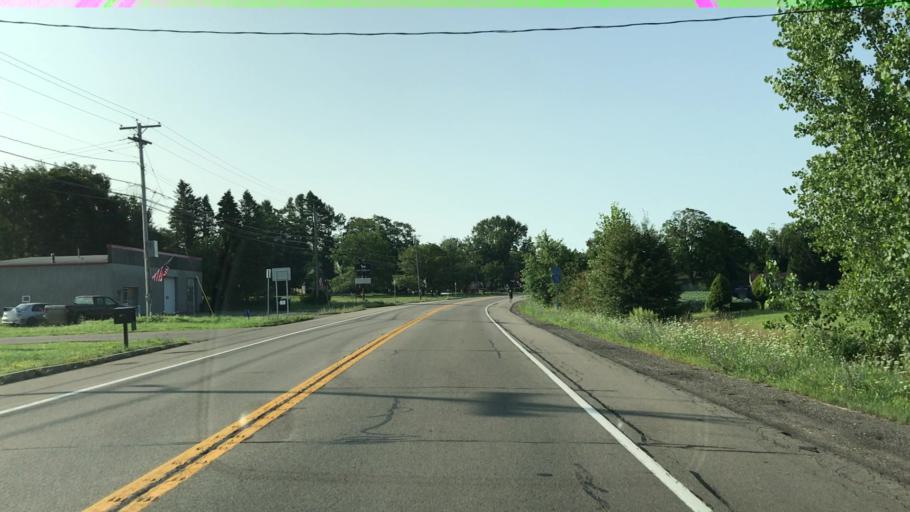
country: US
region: New York
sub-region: Chautauqua County
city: Fredonia
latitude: 42.3506
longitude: -79.3112
